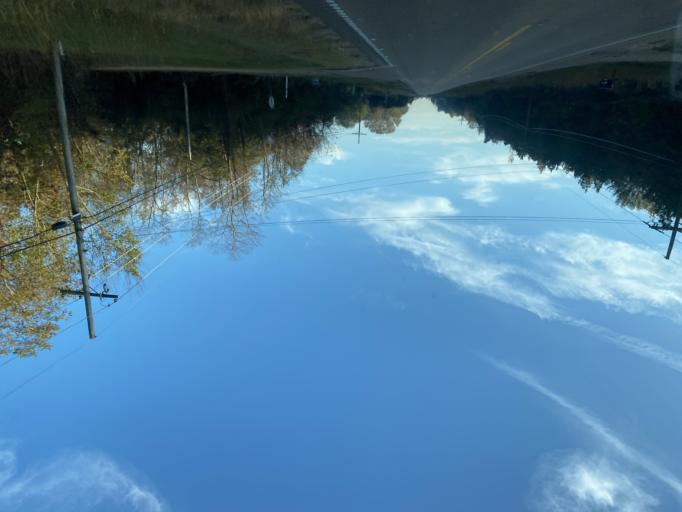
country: US
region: Mississippi
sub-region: Madison County
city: Madison
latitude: 32.4980
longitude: -90.0927
